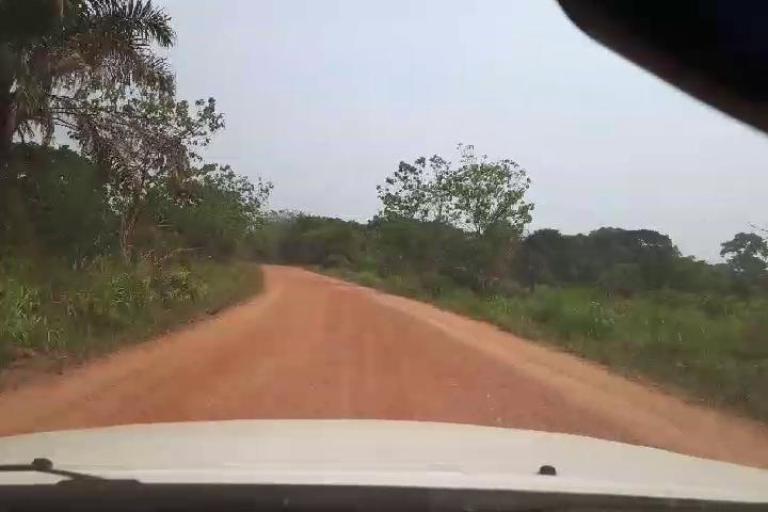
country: SL
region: Northern Province
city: Masingbi
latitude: 8.8801
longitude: -11.8199
